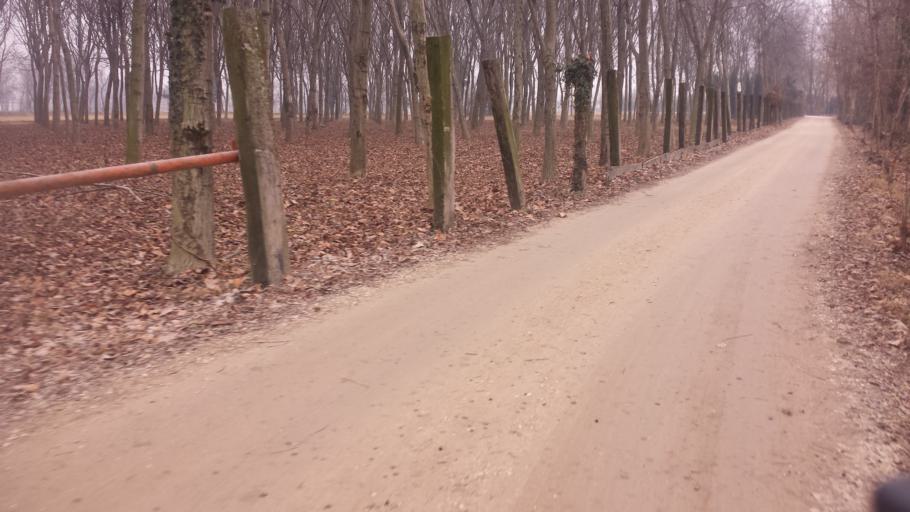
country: IT
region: Veneto
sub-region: Provincia di Vicenza
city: Rosa
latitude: 45.7033
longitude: 11.7564
